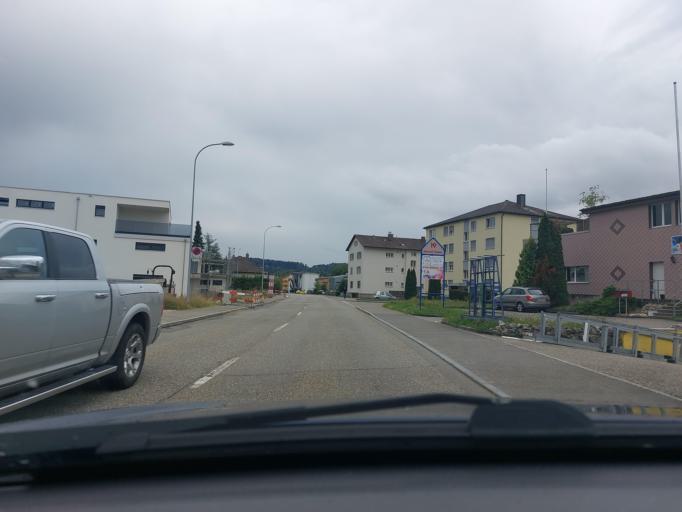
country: CH
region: Solothurn
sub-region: Bezirk Olten
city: Niedergosgen
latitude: 47.3591
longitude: 7.9763
